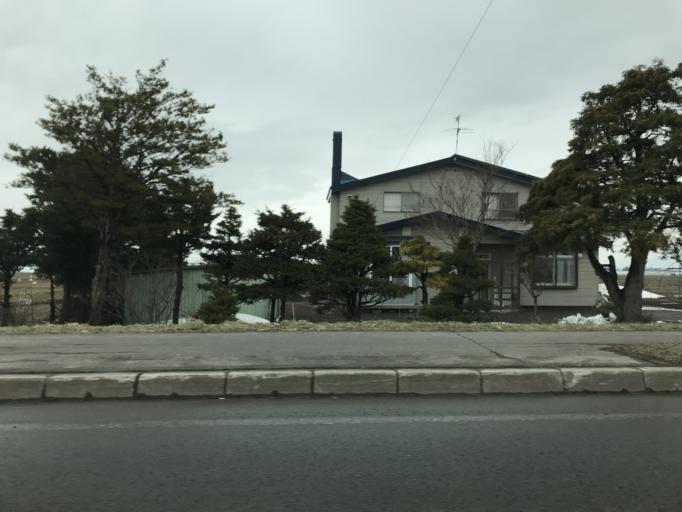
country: JP
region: Hokkaido
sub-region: Asahikawa-shi
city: Asahikawa
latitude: 43.8287
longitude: 142.4213
